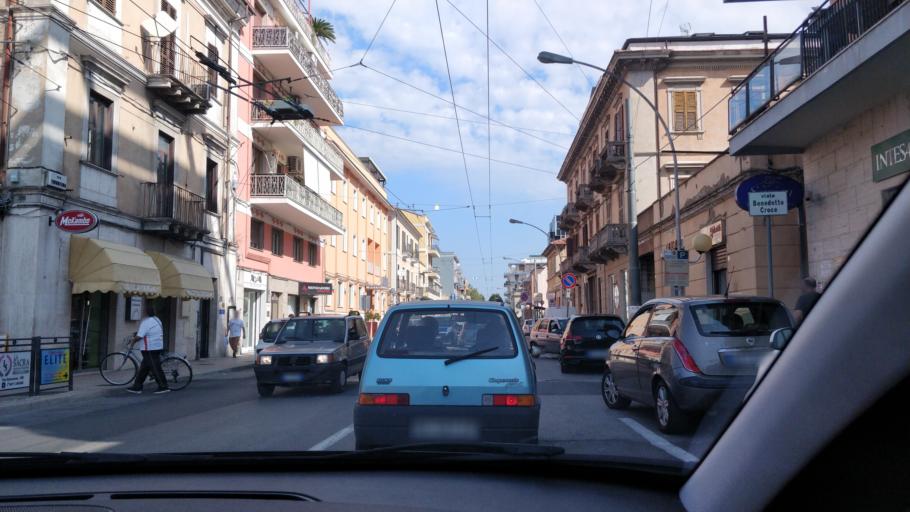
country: IT
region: Abruzzo
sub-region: Provincia di Chieti
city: Chieti
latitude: 42.3571
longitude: 14.1388
